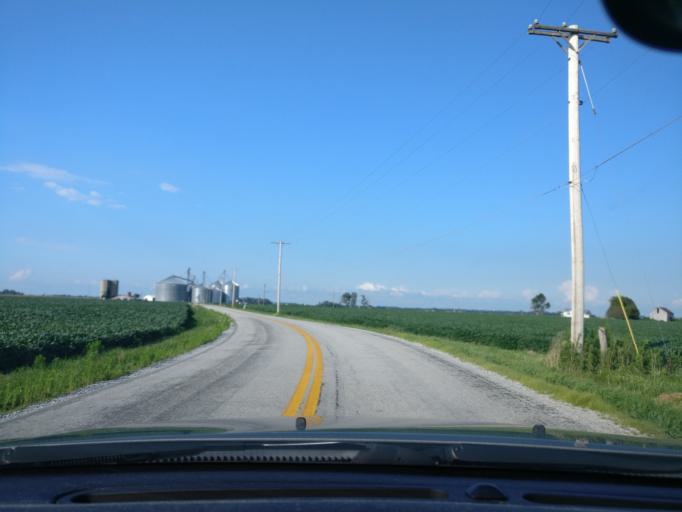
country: US
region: Ohio
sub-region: Greene County
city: Shawnee Hills
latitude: 39.5594
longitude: -83.7741
